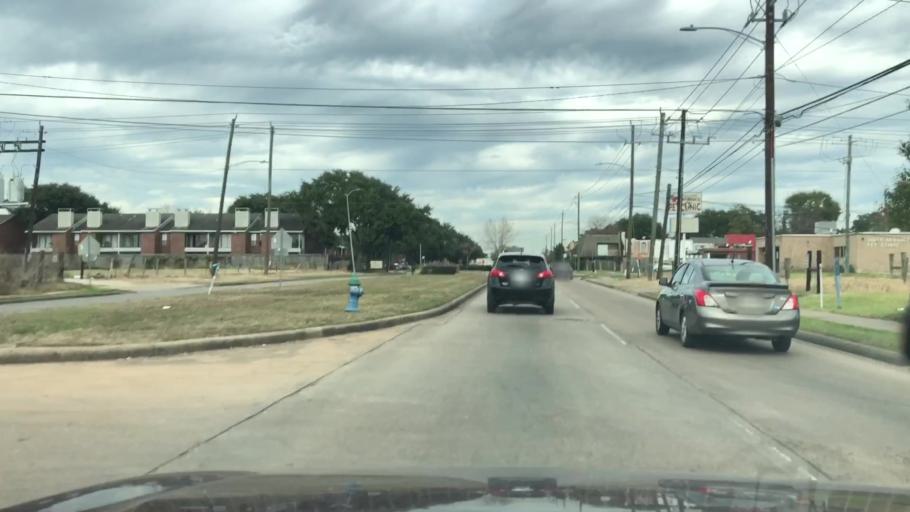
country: US
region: Texas
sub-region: Fort Bend County
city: Missouri City
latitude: 29.6664
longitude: -95.5281
